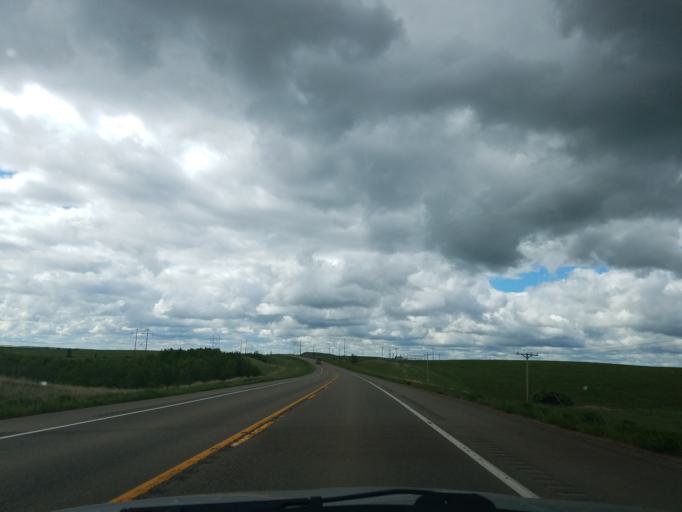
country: US
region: North Dakota
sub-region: McKenzie County
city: Watford City
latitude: 47.4212
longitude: -103.2491
